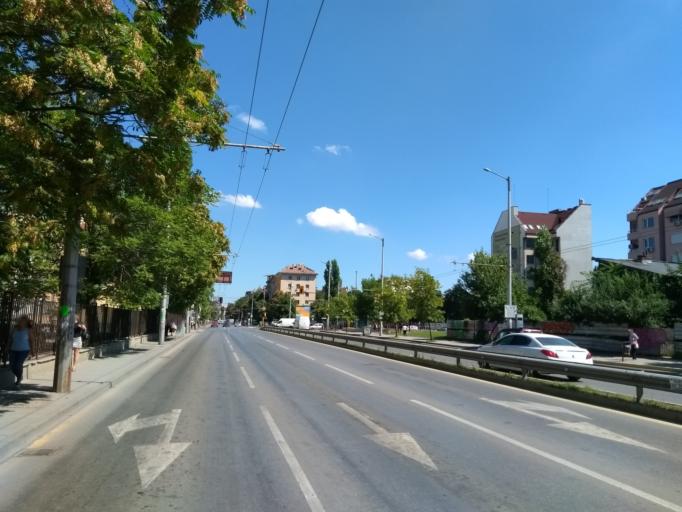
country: BG
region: Sofia-Capital
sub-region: Stolichna Obshtina
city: Sofia
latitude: 42.6988
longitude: 23.3097
